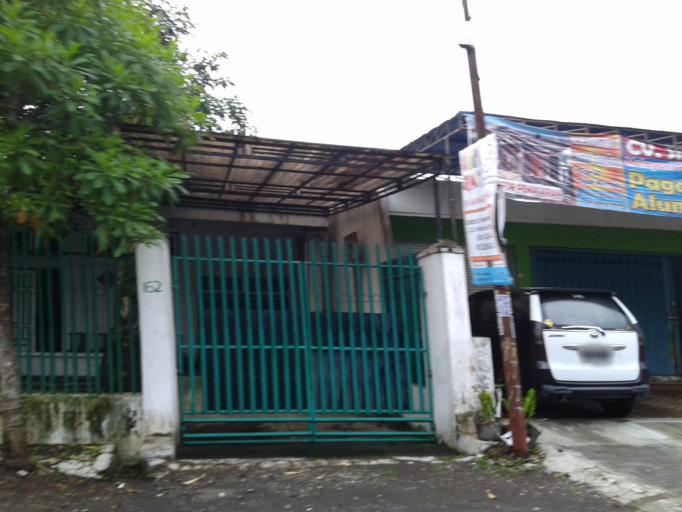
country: ID
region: East Java
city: Singosari
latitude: -7.8861
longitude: 112.6632
